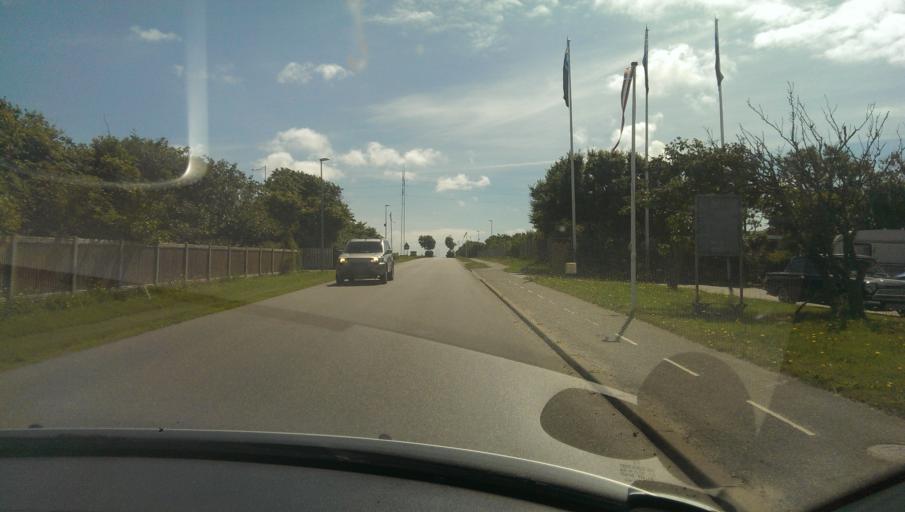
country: DK
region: Central Jutland
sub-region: Ringkobing-Skjern Kommune
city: Ringkobing
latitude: 56.1196
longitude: 8.1773
